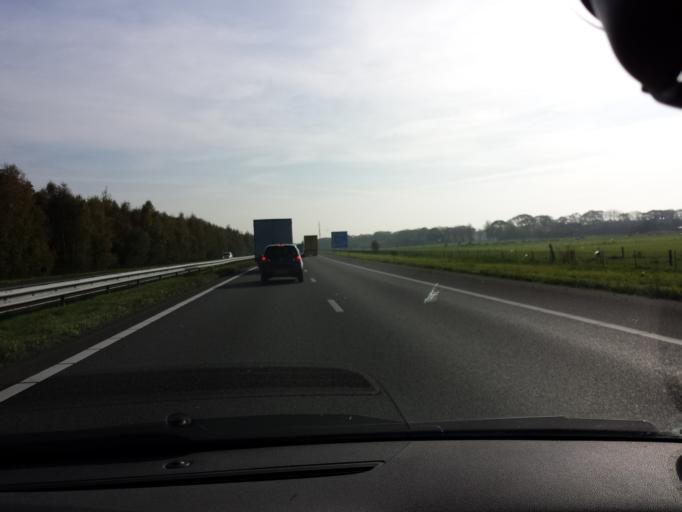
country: NL
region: North Brabant
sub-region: Gemeente Boxmeer
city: Overloon
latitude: 51.5933
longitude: 5.9747
